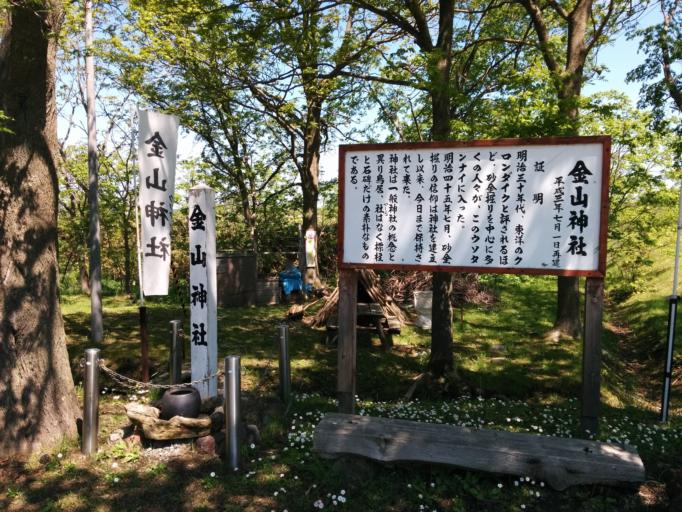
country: JP
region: Hokkaido
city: Makubetsu
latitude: 45.0534
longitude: 142.3556
